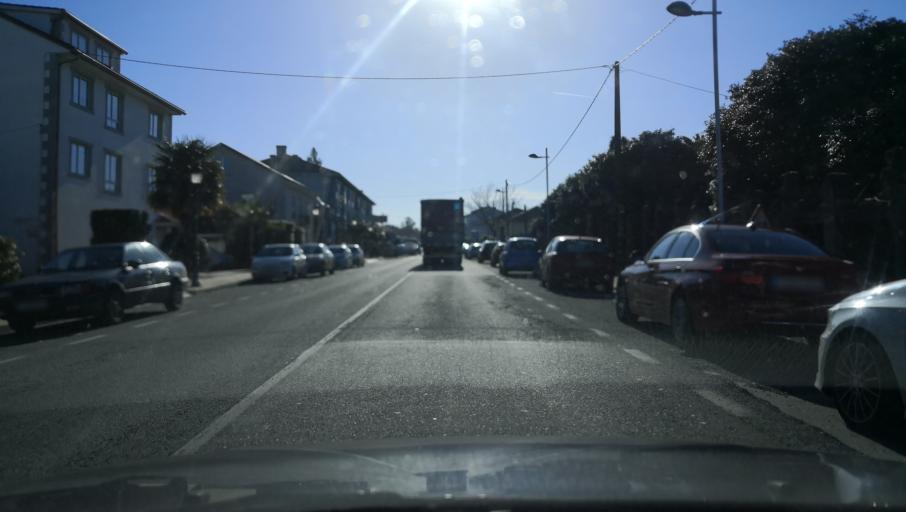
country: ES
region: Galicia
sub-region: Provincia da Coruna
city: Vedra
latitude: 42.7977
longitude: -8.4700
